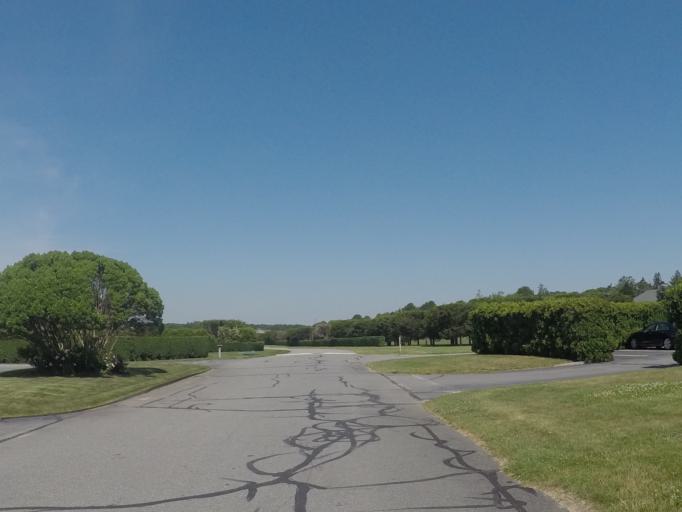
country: US
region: Massachusetts
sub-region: Bristol County
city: Bliss Corner
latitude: 41.5429
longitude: -70.9336
